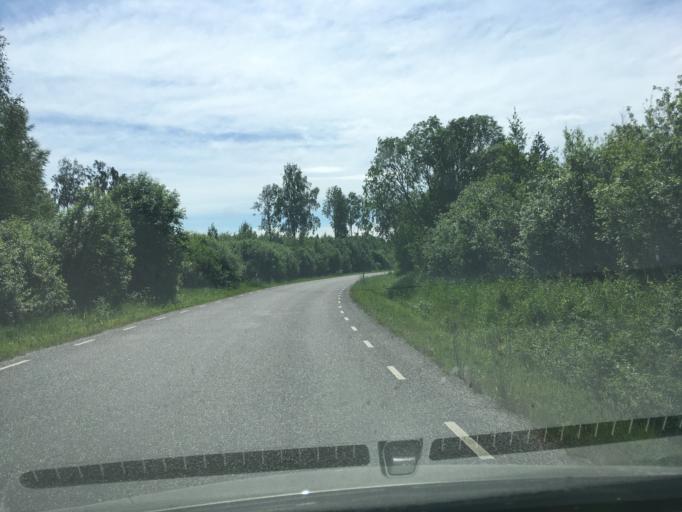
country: EE
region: Paernumaa
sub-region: Audru vald
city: Audru
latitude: 58.4530
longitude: 24.3897
